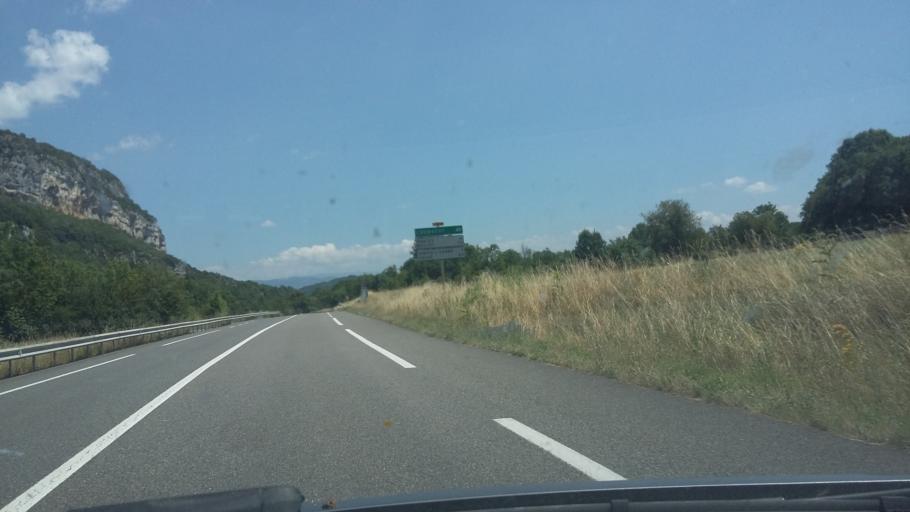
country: FR
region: Rhone-Alpes
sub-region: Departement de l'Ain
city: Virieu-le-Grand
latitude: 45.8234
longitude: 5.6106
